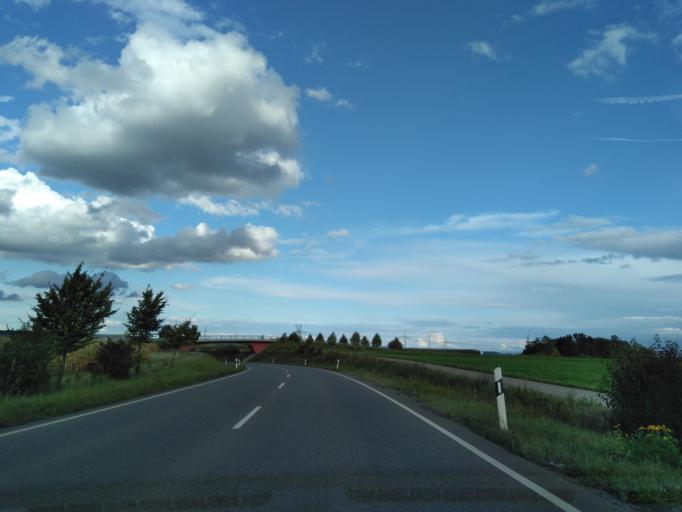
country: DE
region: Baden-Wuerttemberg
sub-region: Regierungsbezirk Stuttgart
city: Bietigheim-Bissingen
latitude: 48.9516
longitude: 9.0735
